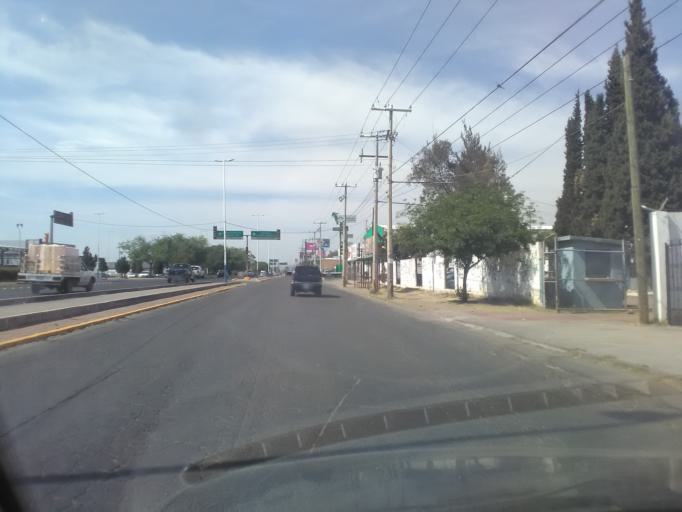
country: MX
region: Durango
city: Victoria de Durango
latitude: 24.0487
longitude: -104.6221
